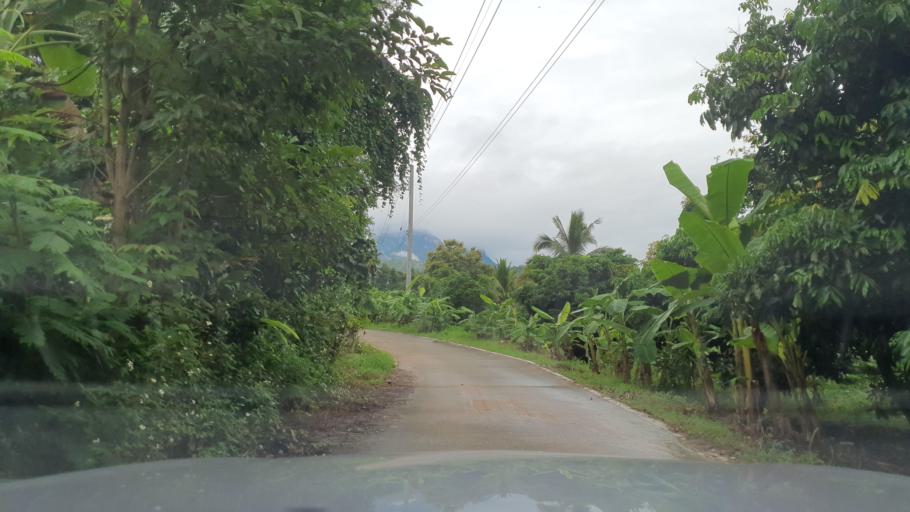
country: TH
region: Chiang Mai
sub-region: Amphoe Chiang Dao
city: Chiang Dao
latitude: 19.3328
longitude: 98.9285
